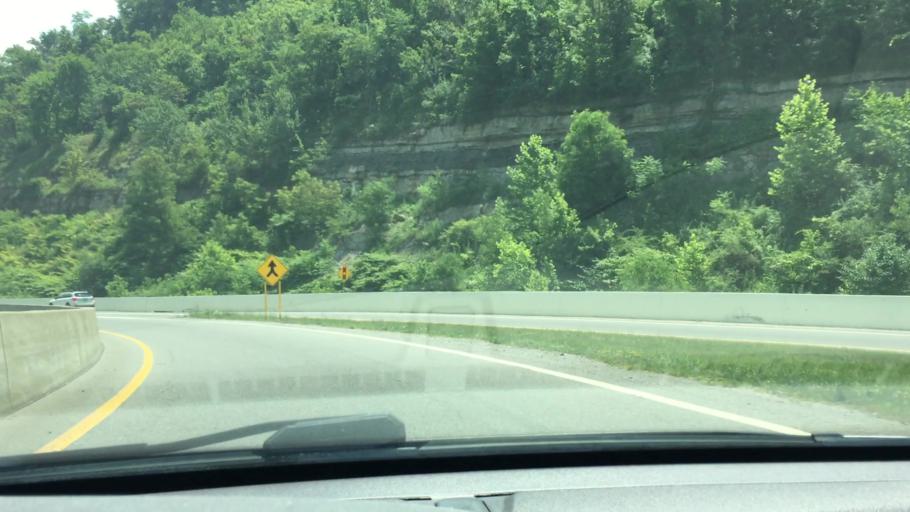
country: US
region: Ohio
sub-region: Belmont County
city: Bridgeport
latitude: 40.0480
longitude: -80.7369
